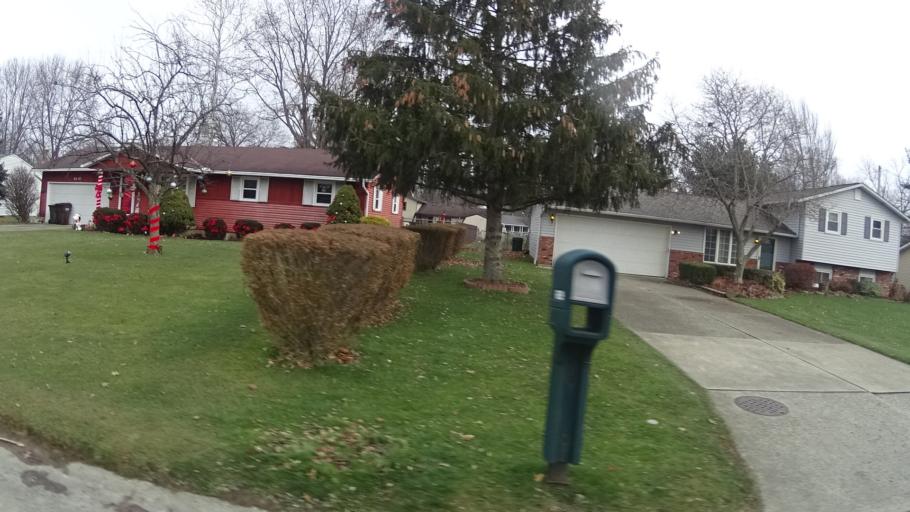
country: US
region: Ohio
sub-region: Lorain County
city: Amherst
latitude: 41.4031
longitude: -82.1863
